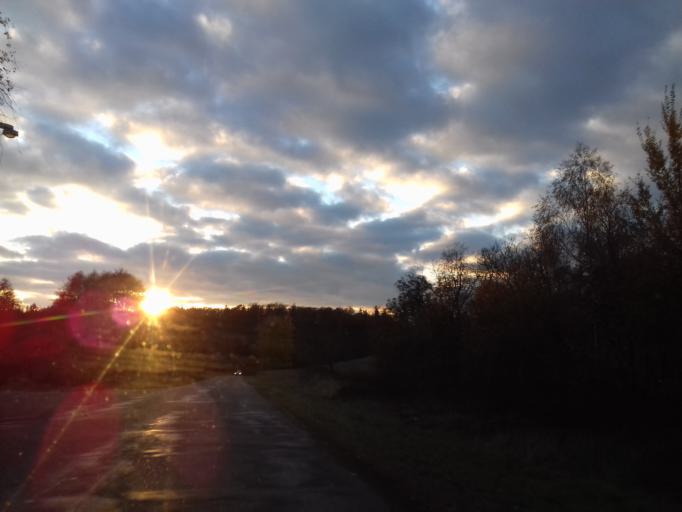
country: CZ
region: Pardubicky
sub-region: Okres Chrudim
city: Skutec
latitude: 49.8329
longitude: 15.9827
